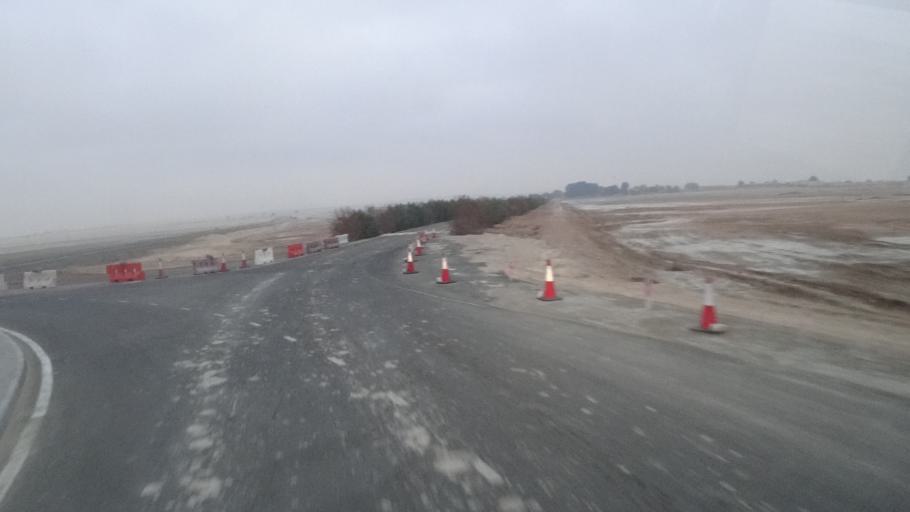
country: AE
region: Abu Dhabi
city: Abu Dhabi
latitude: 24.1922
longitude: 54.6996
